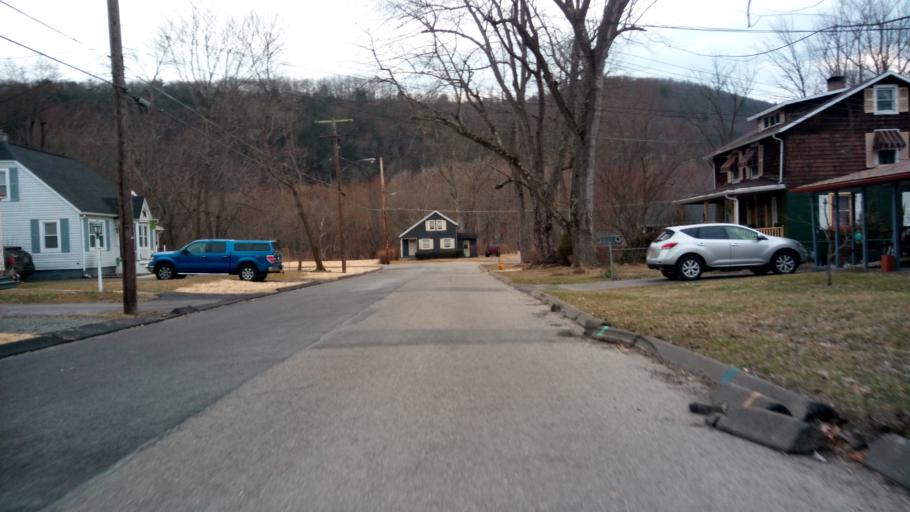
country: US
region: New York
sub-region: Chemung County
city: West Elmira
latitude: 42.0796
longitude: -76.8589
